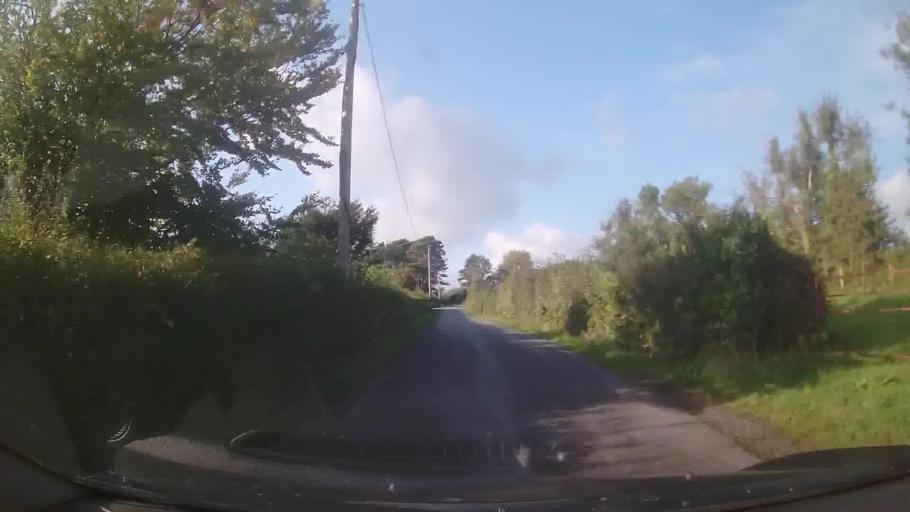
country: GB
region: Wales
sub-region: Pembrokeshire
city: Saundersfoot
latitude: 51.7546
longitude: -4.6504
